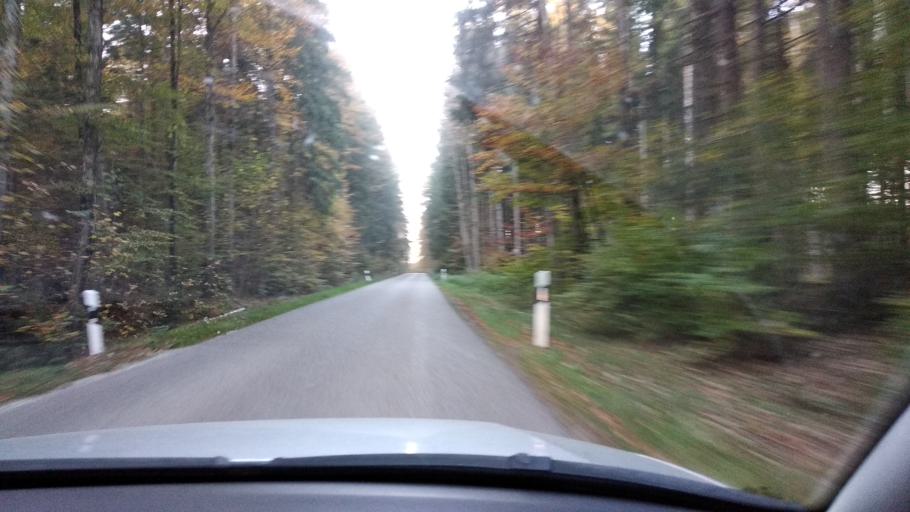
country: DE
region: Bavaria
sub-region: Upper Bavaria
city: Egmating
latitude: 47.9857
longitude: 11.8159
